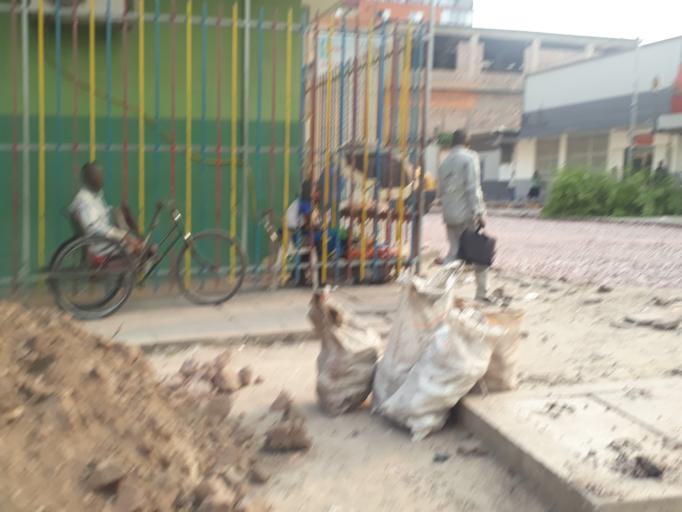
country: CD
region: Kinshasa
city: Kinshasa
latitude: -4.3006
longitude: 15.3110
